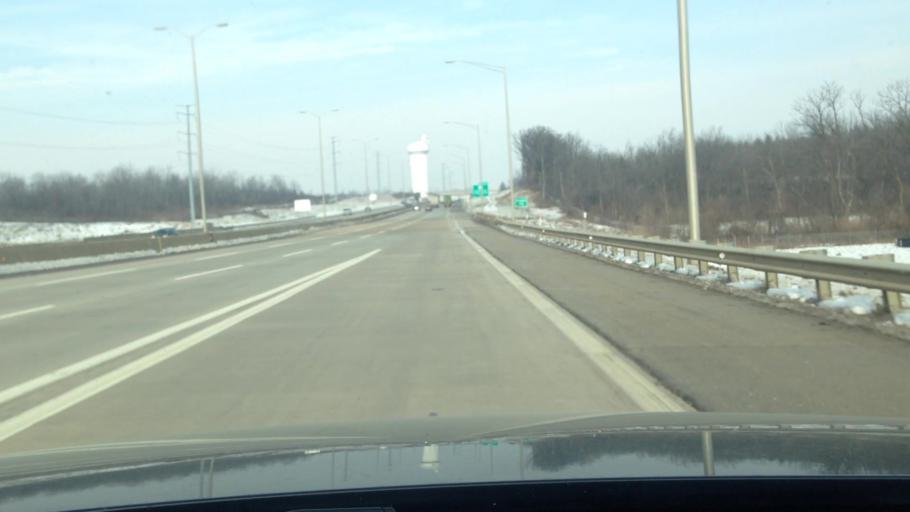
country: US
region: Illinois
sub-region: Will County
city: Lockport
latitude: 41.6043
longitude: -88.0121
